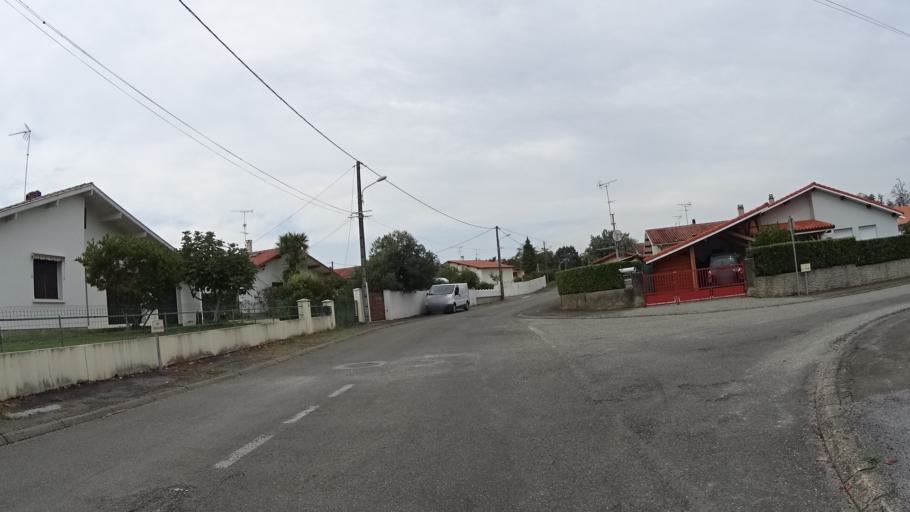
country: FR
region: Aquitaine
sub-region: Departement des Landes
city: Saint-Paul-les-Dax
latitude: 43.7283
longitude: -1.0725
